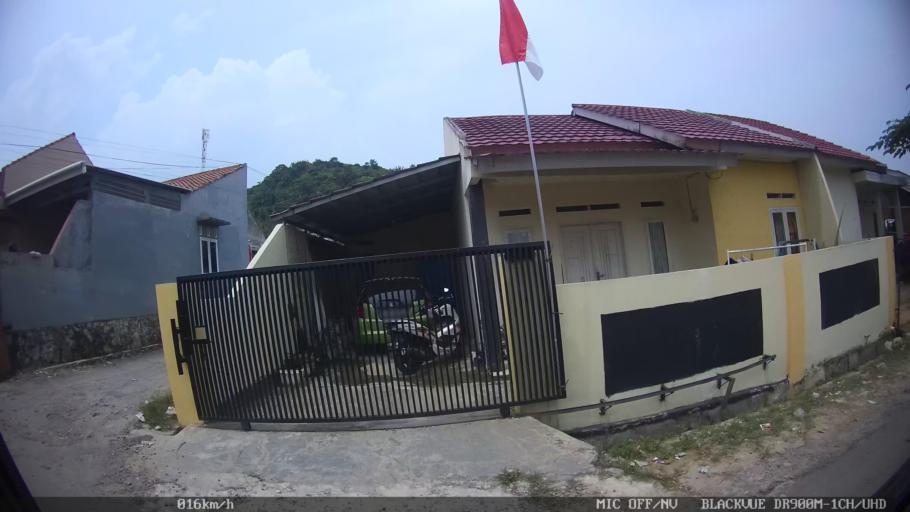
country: ID
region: Lampung
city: Kedaton
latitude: -5.4017
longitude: 105.3237
